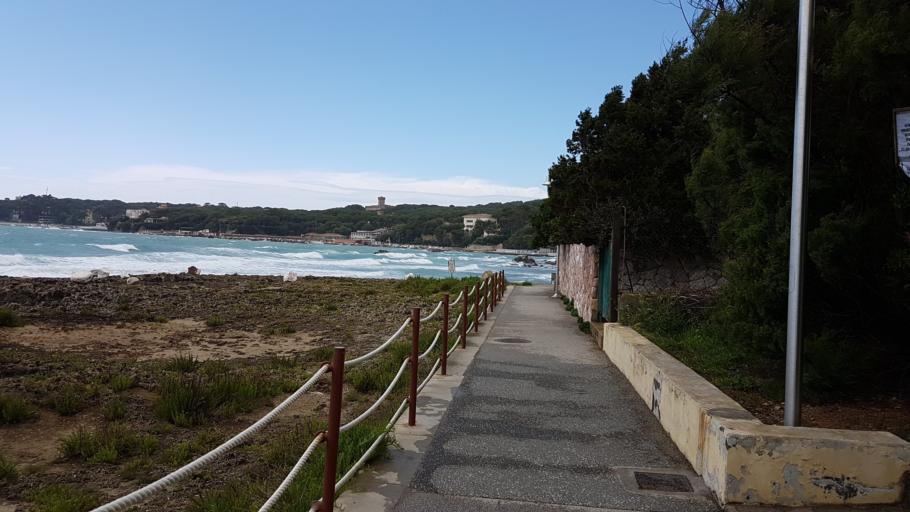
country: IT
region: Tuscany
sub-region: Provincia di Livorno
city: Rosignano Solvay-Castiglioncello
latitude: 43.4007
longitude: 10.4220
